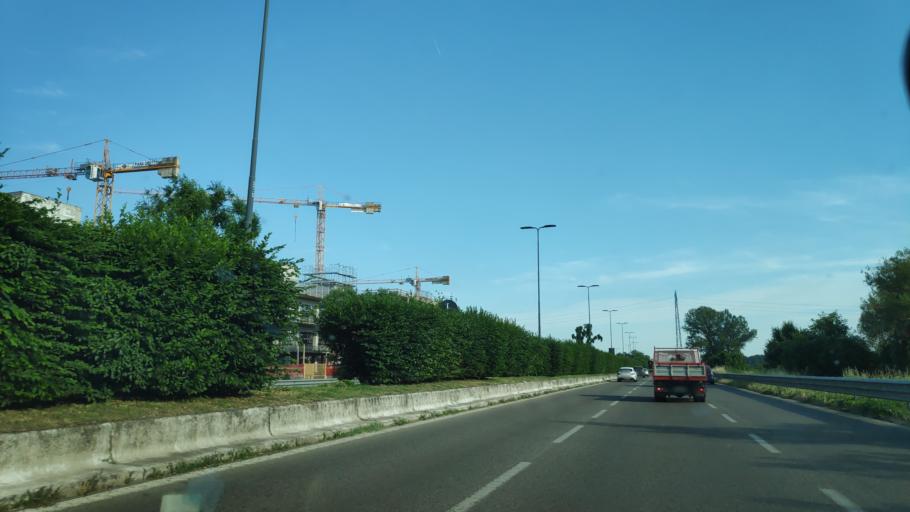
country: IT
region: Lombardy
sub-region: Citta metropolitana di Milano
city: Noverasco-Sporting Mirasole
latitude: 45.4257
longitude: 9.1968
